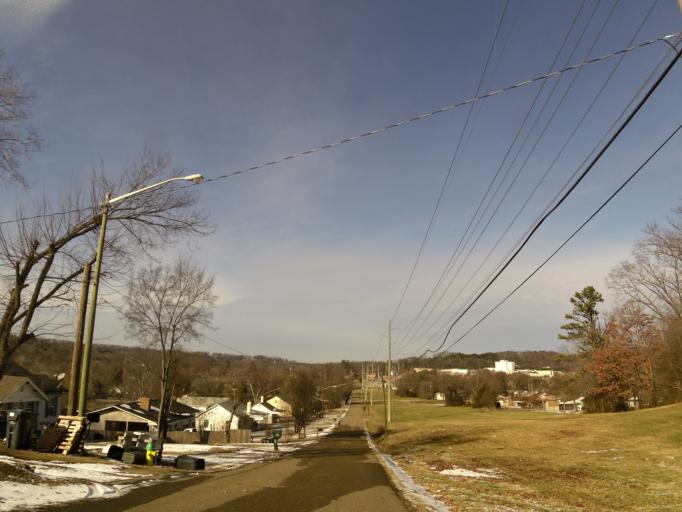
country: US
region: Tennessee
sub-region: Knox County
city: Knoxville
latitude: 35.9683
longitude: -83.9730
